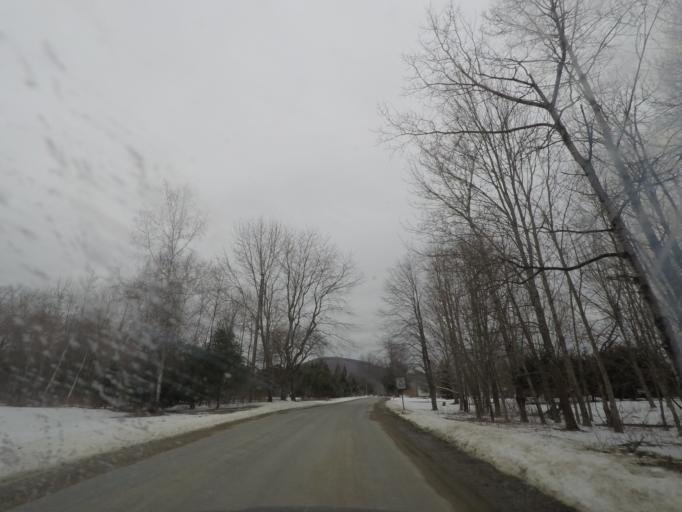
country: US
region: Massachusetts
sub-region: Berkshire County
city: Richmond
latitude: 42.5404
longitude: -73.4090
